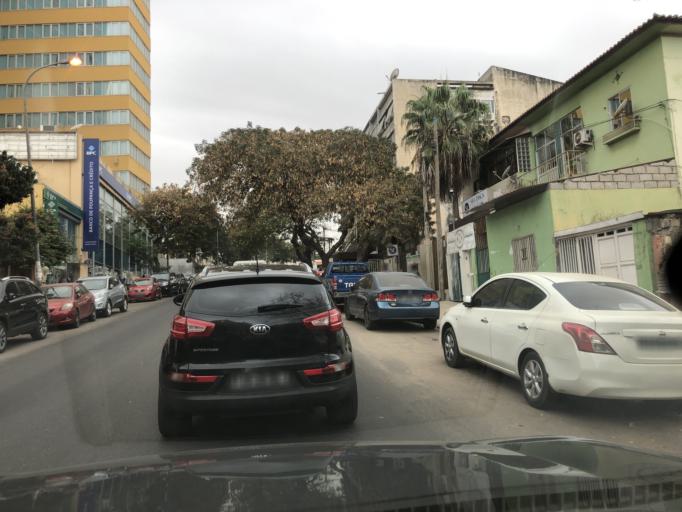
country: AO
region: Luanda
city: Luanda
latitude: -8.8246
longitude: 13.2329
